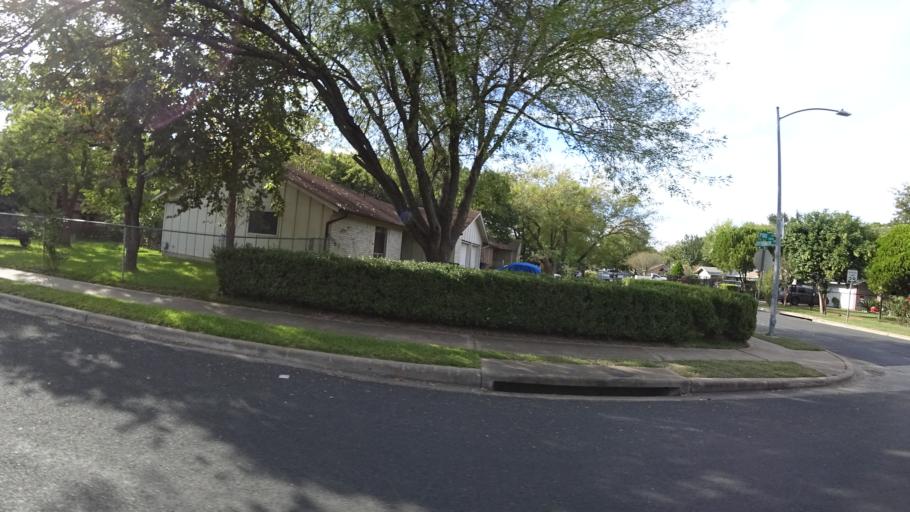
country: US
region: Texas
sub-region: Travis County
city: Onion Creek
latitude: 30.1887
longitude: -97.7508
